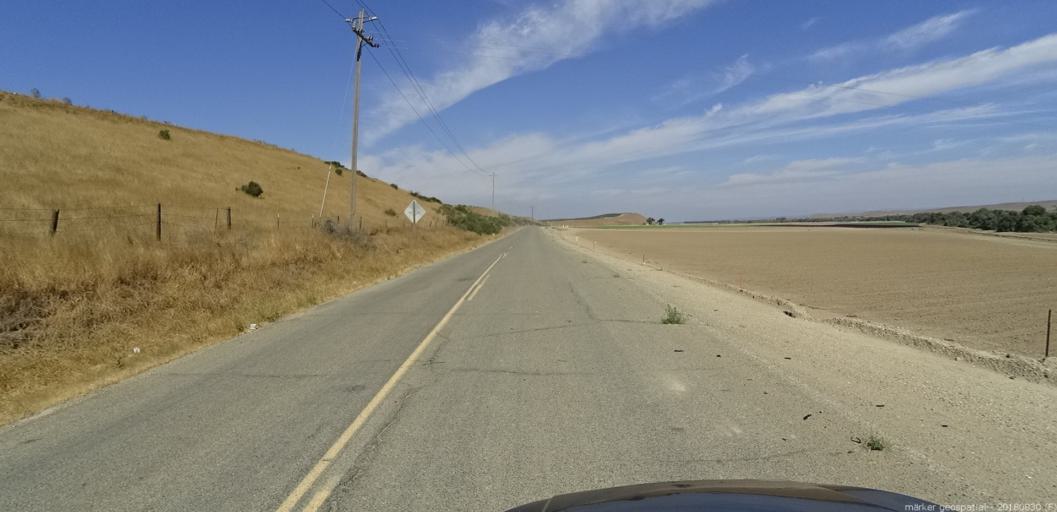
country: US
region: California
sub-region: Monterey County
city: King City
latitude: 36.1059
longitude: -121.0273
